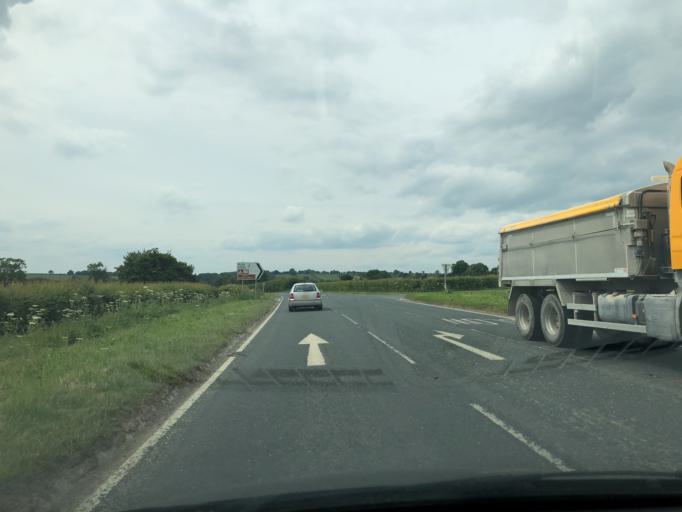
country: GB
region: England
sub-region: North Yorkshire
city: Pickering
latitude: 54.2621
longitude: -0.8153
